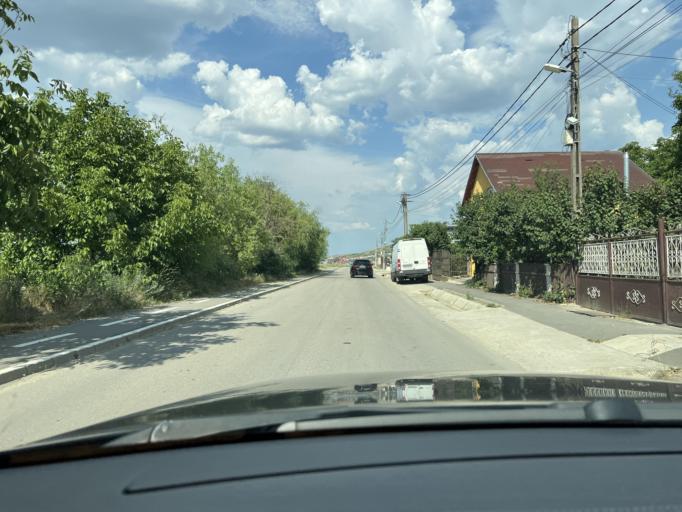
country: RO
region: Cluj
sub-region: Comuna Apahida
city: Dezmir
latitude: 46.7773
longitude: 23.7086
